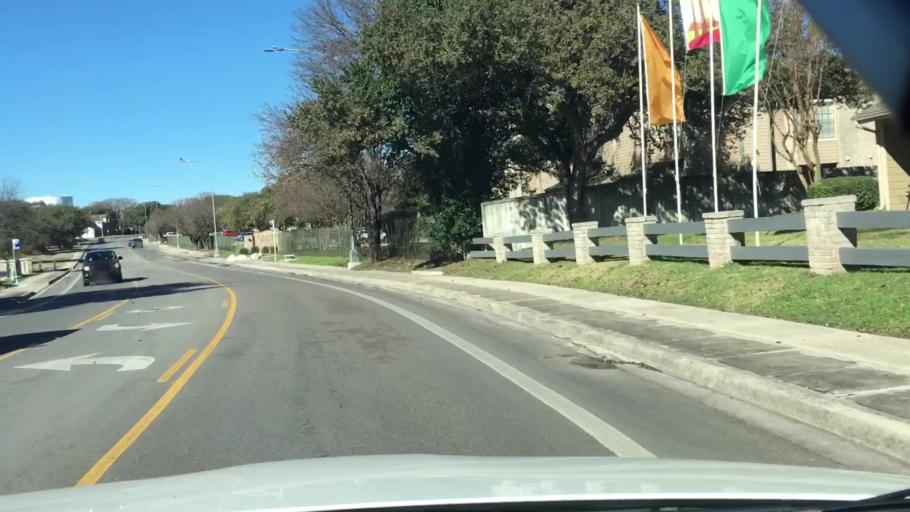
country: US
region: Texas
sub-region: Bexar County
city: Hollywood Park
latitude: 29.5917
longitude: -98.4495
